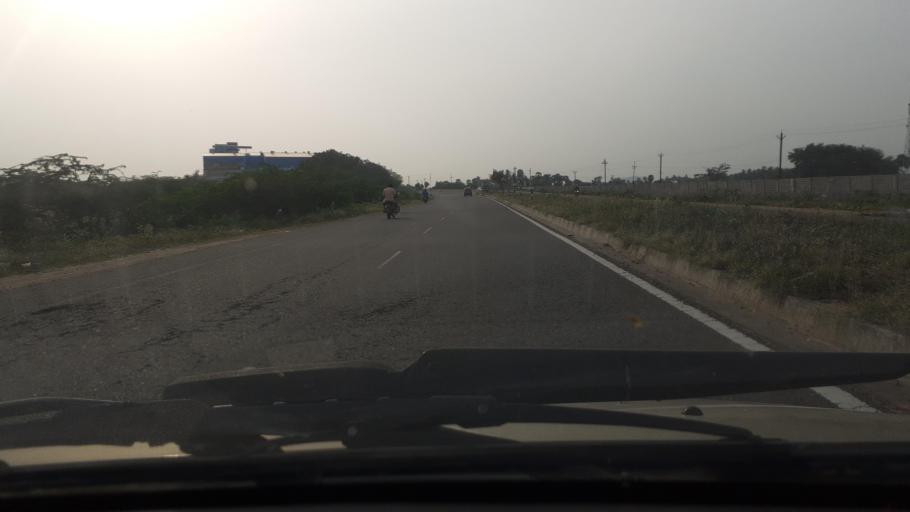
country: IN
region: Tamil Nadu
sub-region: Tirunelveli Kattabo
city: Tirunelveli
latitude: 8.7089
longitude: 77.8098
